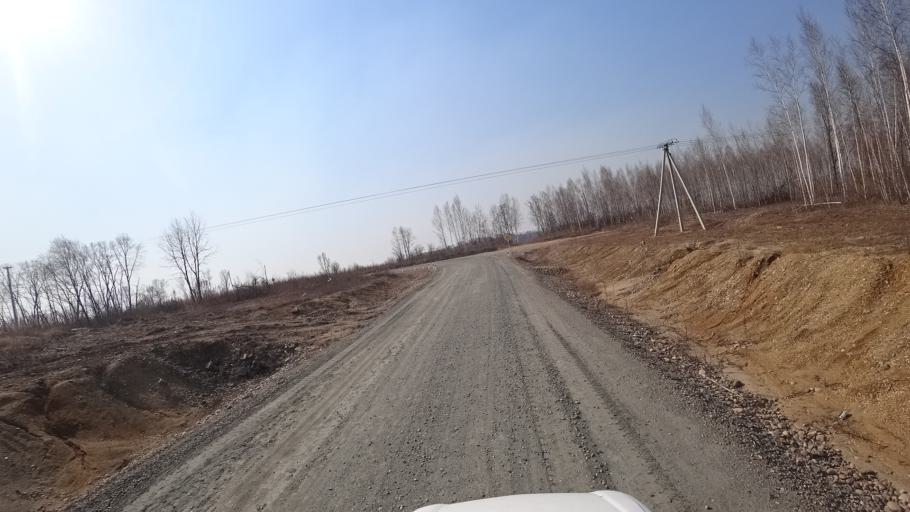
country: RU
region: Amur
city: Novobureyskiy
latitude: 49.8276
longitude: 129.9896
